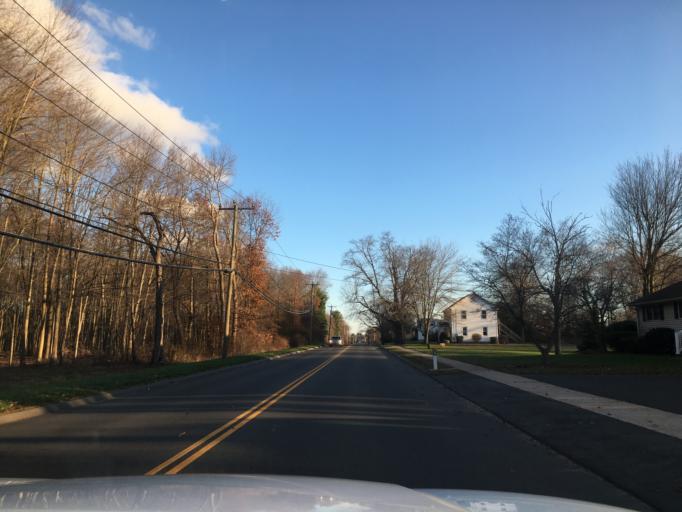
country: US
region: Connecticut
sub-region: Hartford County
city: Enfield
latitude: 41.9690
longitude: -72.5866
